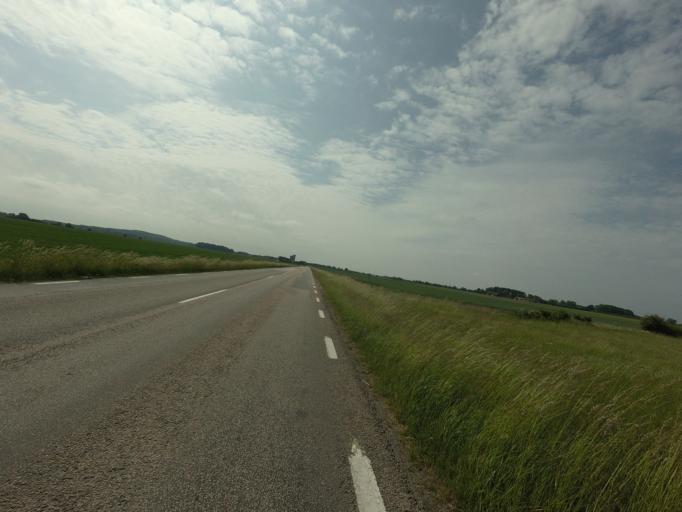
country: SE
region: Skane
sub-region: Helsingborg
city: Odakra
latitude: 56.1905
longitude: 12.6755
